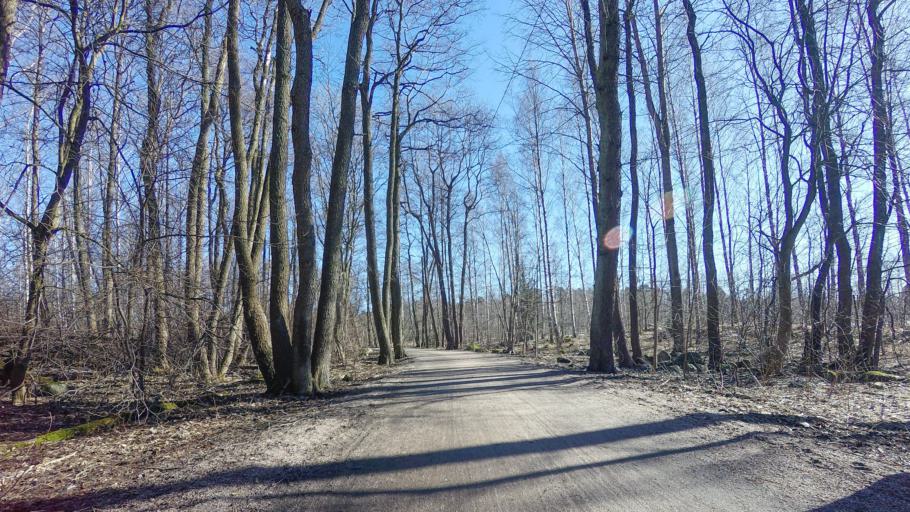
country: FI
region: Uusimaa
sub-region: Helsinki
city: Vantaa
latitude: 60.1939
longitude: 25.0598
